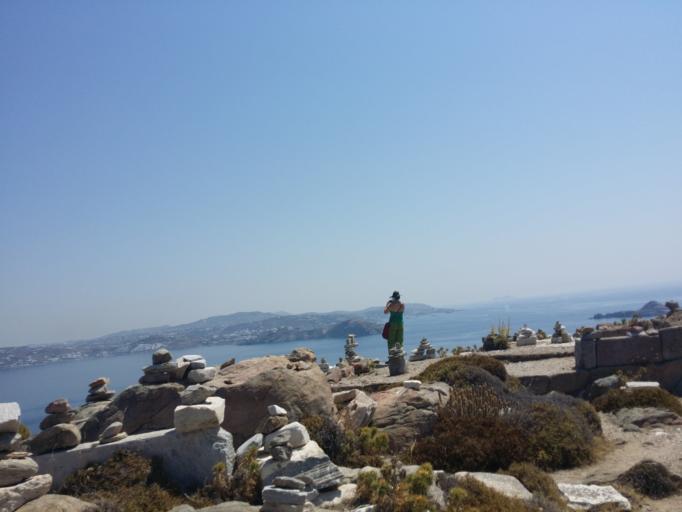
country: GR
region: South Aegean
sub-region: Nomos Kykladon
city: Mykonos
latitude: 37.3955
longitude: 25.2725
